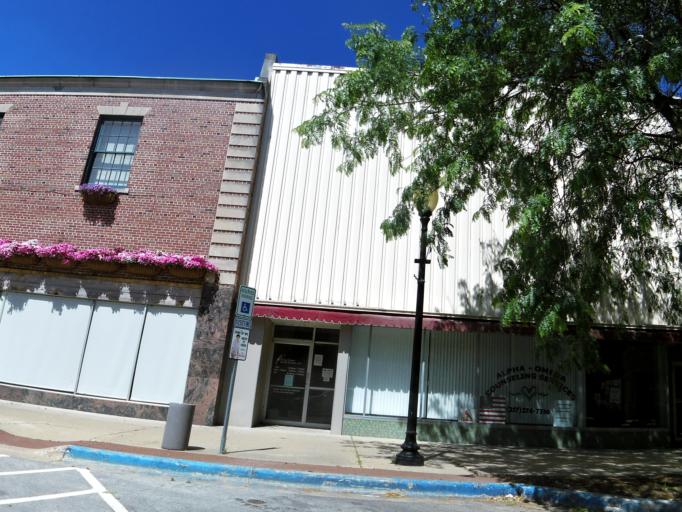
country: US
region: Illinois
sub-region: Vermilion County
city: Danville
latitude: 40.1270
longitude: -87.6300
